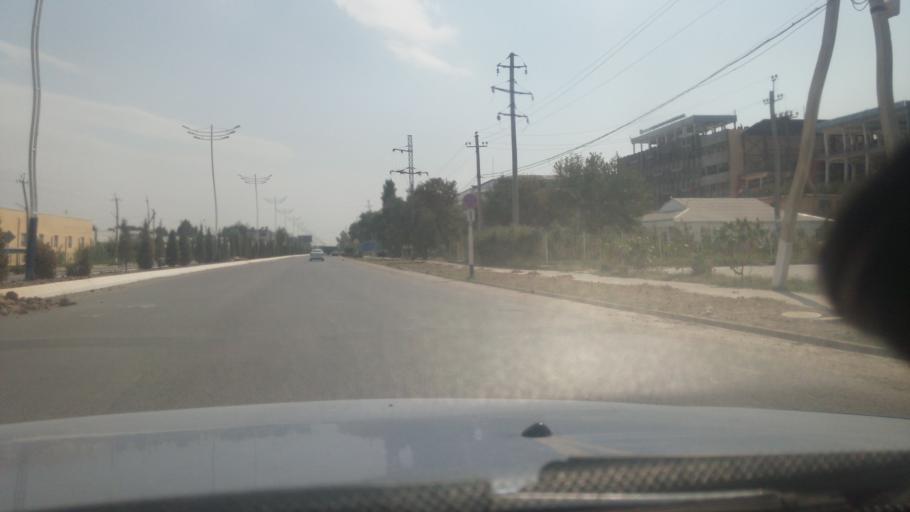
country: UZ
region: Sirdaryo
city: Guliston
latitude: 40.5198
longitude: 68.7680
